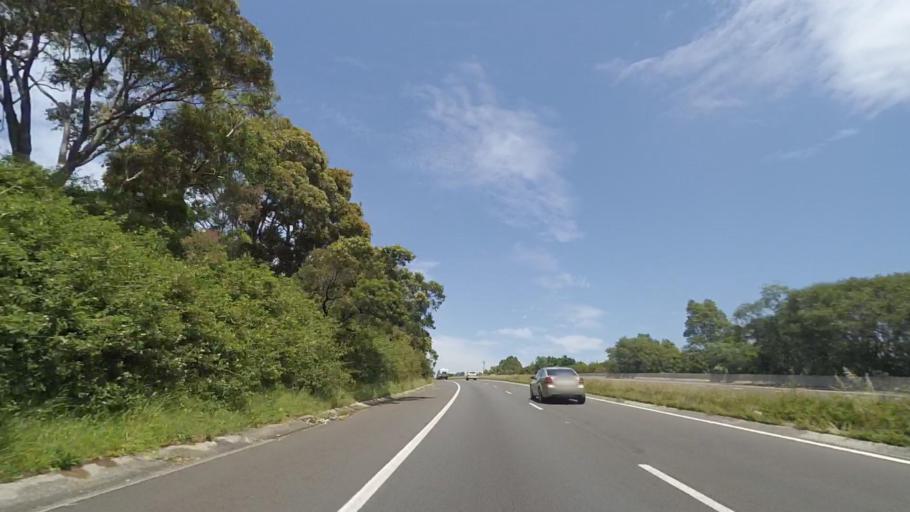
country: AU
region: New South Wales
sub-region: Kiama
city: Kiama
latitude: -34.6716
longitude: 150.8433
